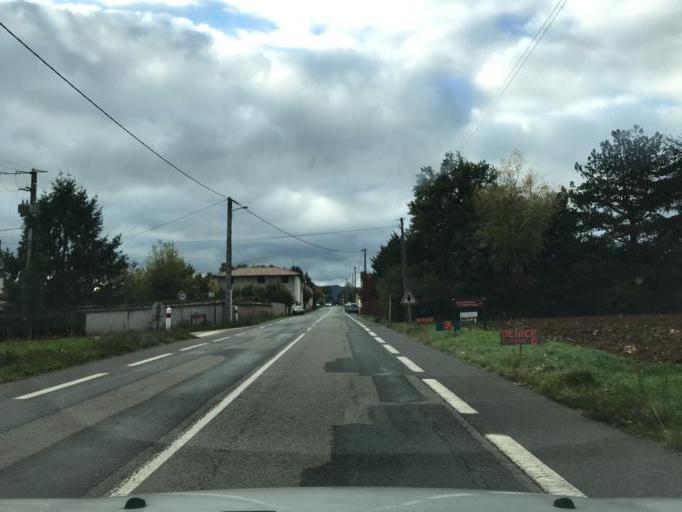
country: FR
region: Rhone-Alpes
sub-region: Departement du Rhone
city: Gleize
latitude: 45.9940
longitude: 4.6805
